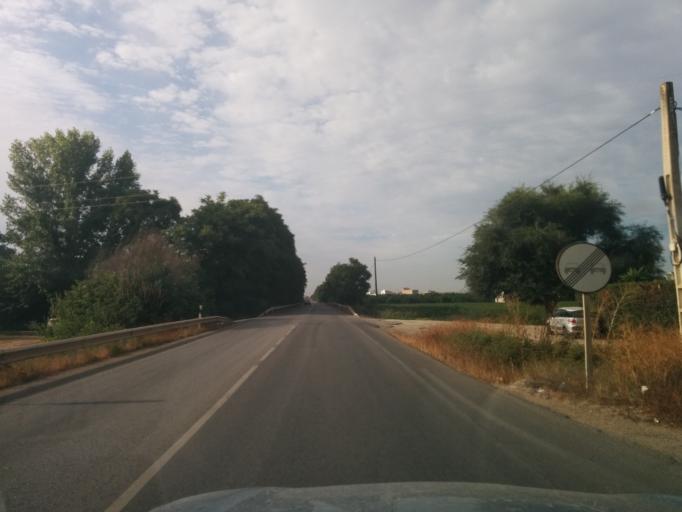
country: ES
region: Andalusia
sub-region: Provincia de Sevilla
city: La Algaba
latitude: 37.4774
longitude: -6.0089
